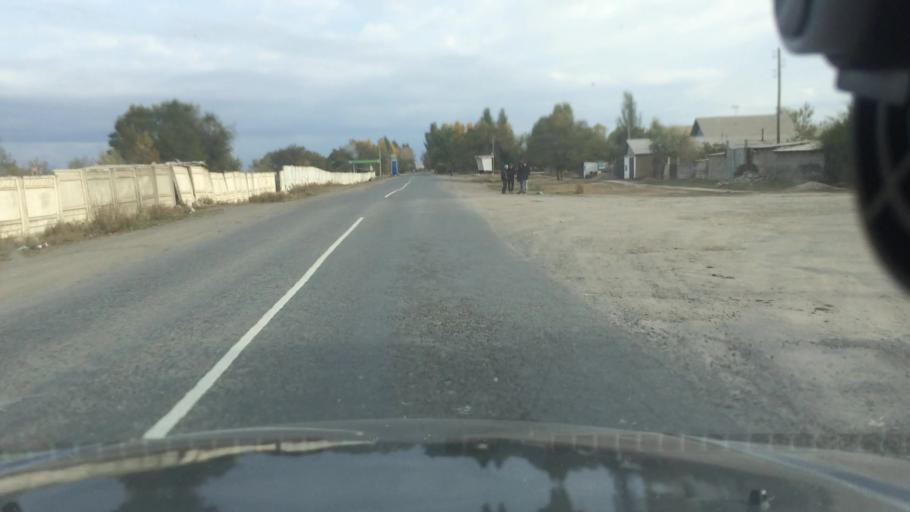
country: KG
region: Ysyk-Koel
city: Karakol
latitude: 42.5375
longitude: 78.3824
